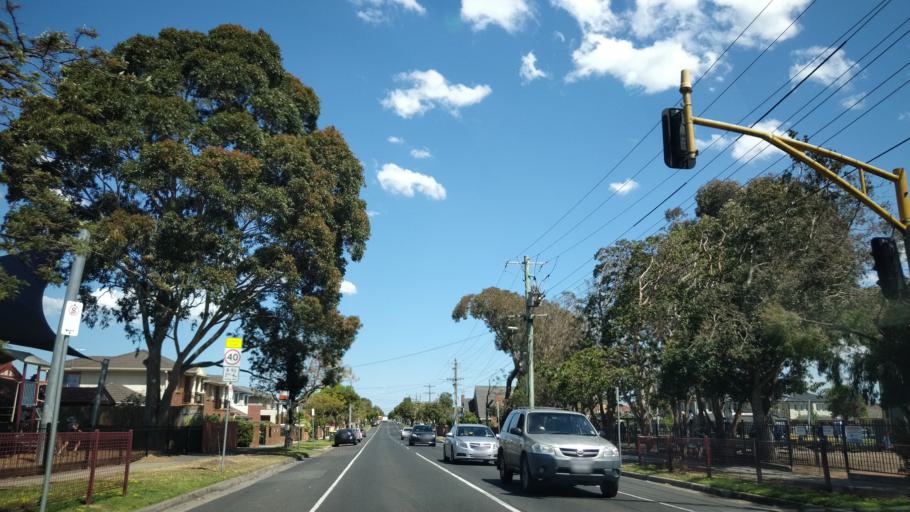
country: AU
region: Victoria
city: McKinnon
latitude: -37.9079
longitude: 145.0531
